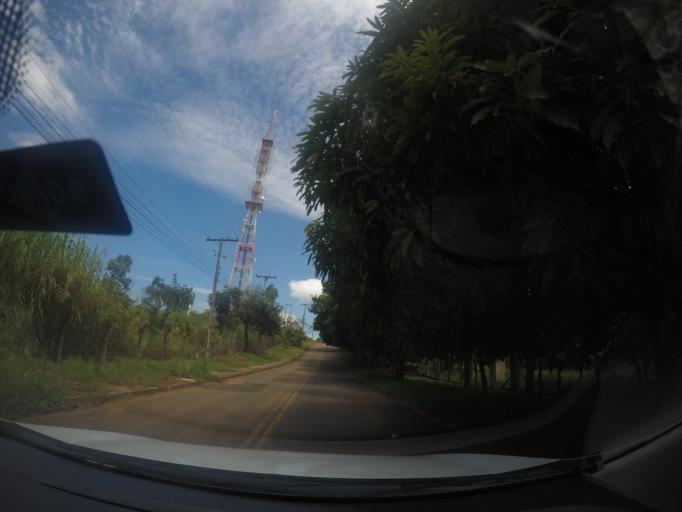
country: BR
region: Goias
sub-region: Goiania
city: Goiania
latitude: -16.6647
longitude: -49.3438
